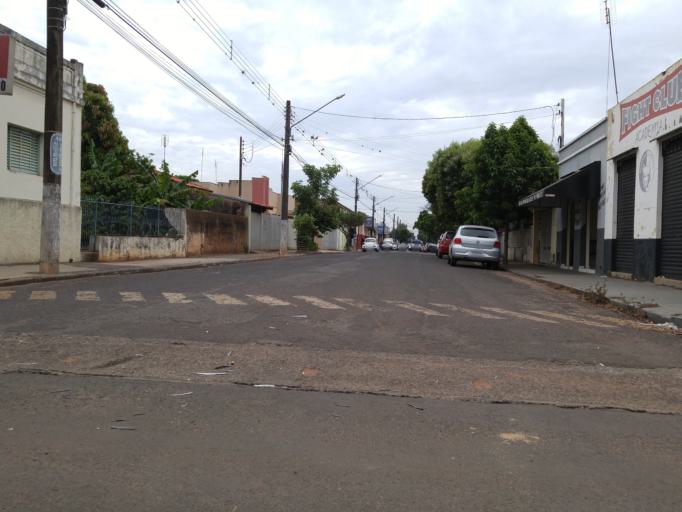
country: BR
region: Sao Paulo
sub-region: Paraguacu Paulista
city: Paraguacu Paulista
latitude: -22.4197
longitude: -50.5759
